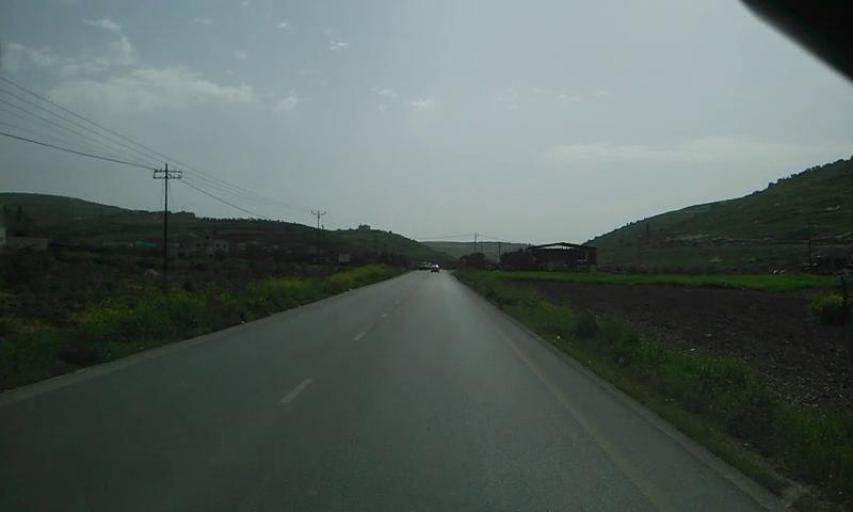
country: PS
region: West Bank
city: Mirkah
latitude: 32.3949
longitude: 35.2210
